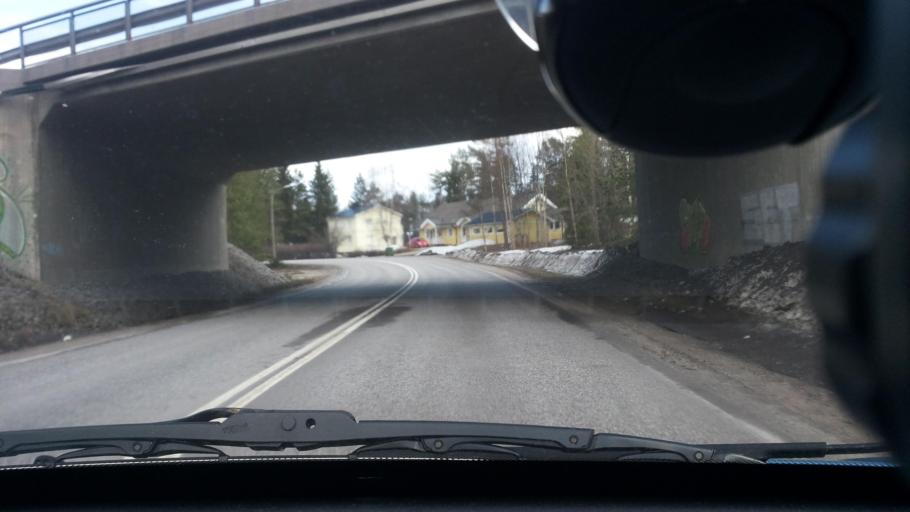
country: SE
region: Norrbotten
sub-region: Lulea Kommun
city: Gammelstad
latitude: 65.5877
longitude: 22.0165
